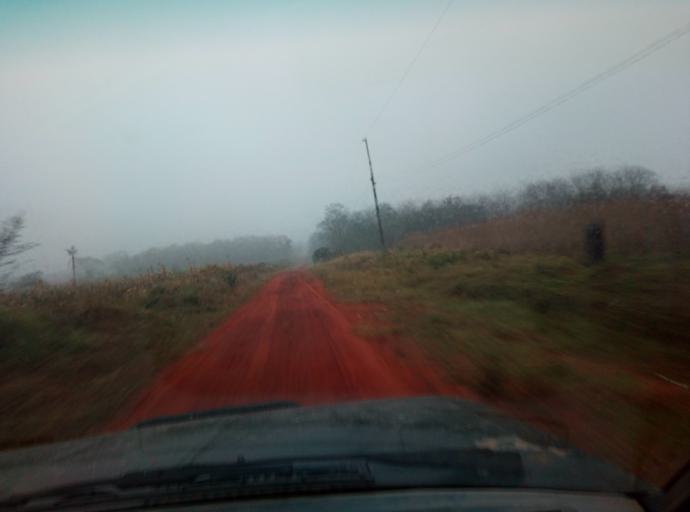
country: PY
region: Caaguazu
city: Doctor Cecilio Baez
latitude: -25.1572
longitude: -56.2745
